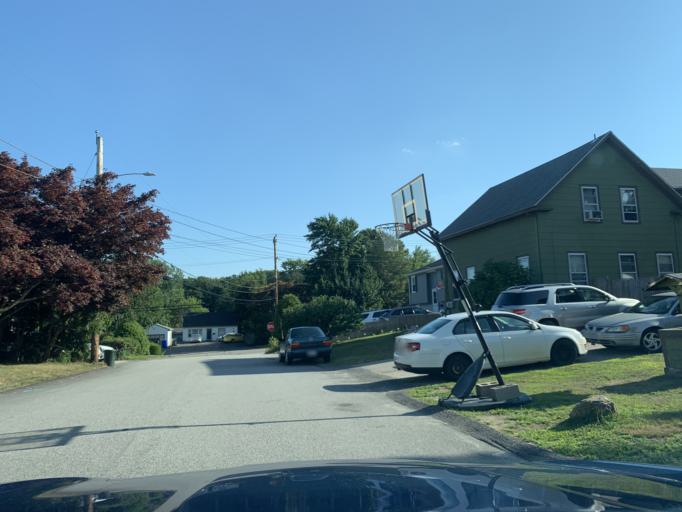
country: US
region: Rhode Island
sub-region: Kent County
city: West Warwick
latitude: 41.6854
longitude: -71.5136
